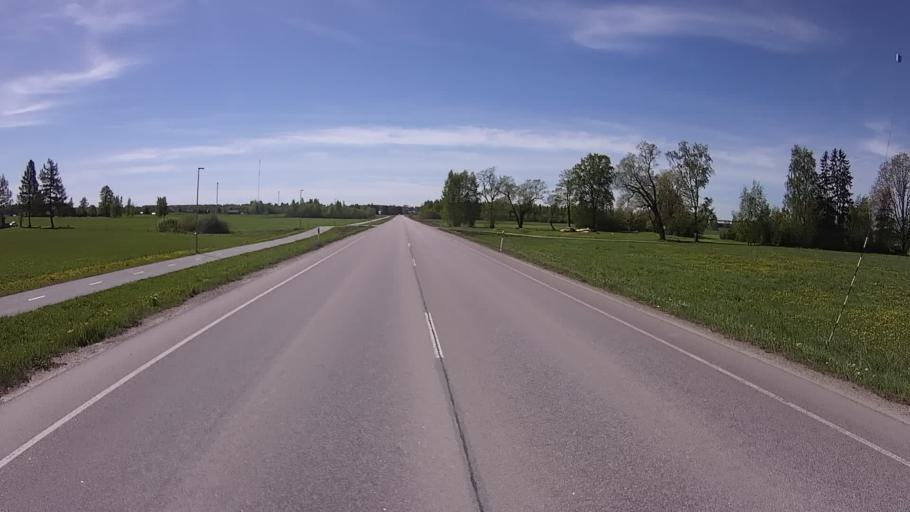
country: EE
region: Polvamaa
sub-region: Polva linn
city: Polva
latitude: 58.0808
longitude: 27.0898
